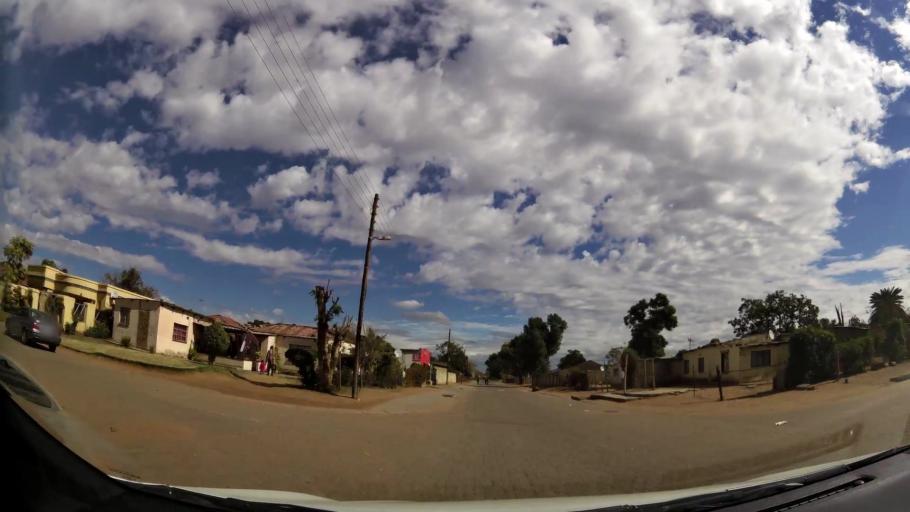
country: ZA
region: Limpopo
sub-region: Waterberg District Municipality
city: Bela-Bela
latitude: -24.8881
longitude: 28.3139
